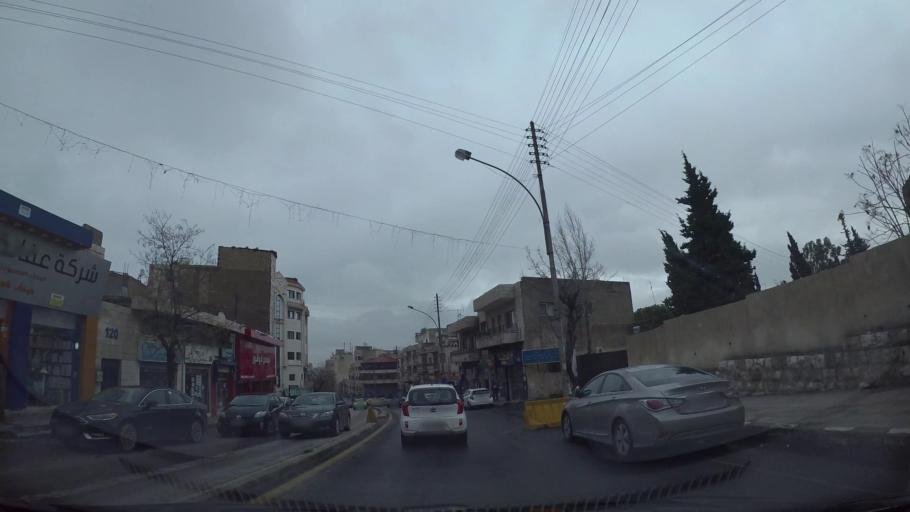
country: JO
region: Amman
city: Amman
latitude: 31.9633
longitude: 35.9234
